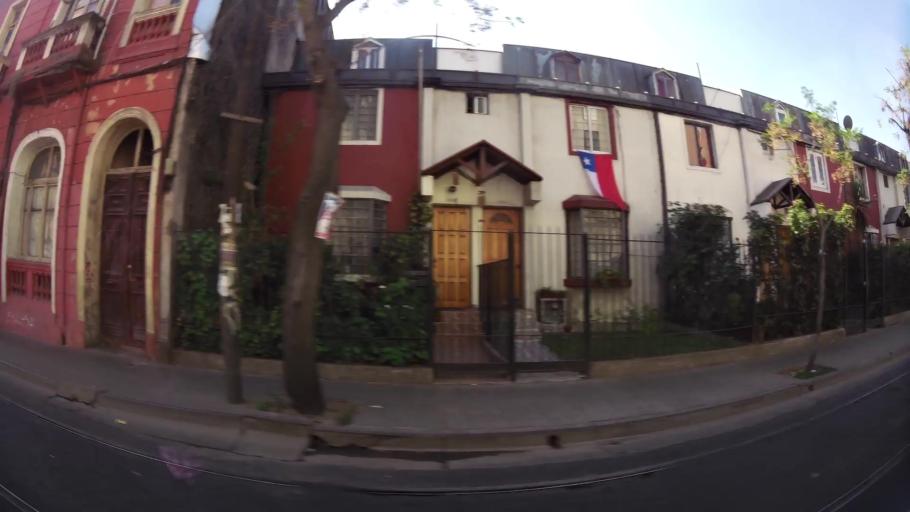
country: CL
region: Santiago Metropolitan
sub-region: Provincia de Santiago
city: Santiago
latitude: -33.4396
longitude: -70.6730
